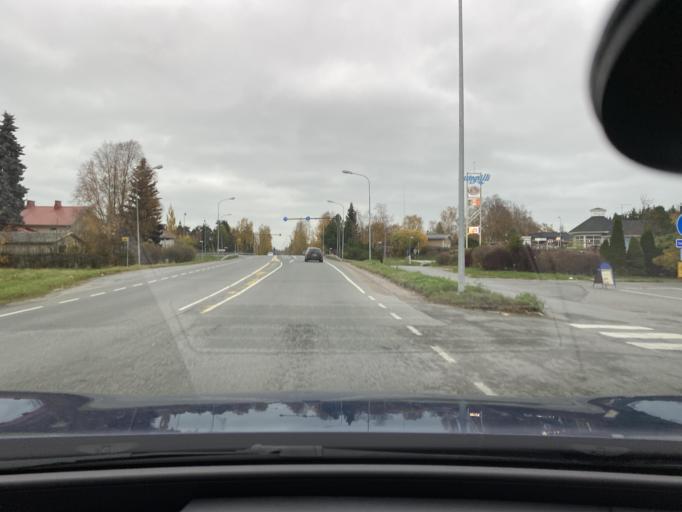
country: FI
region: Varsinais-Suomi
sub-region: Vakka-Suomi
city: Laitila
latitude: 60.8750
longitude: 21.6996
